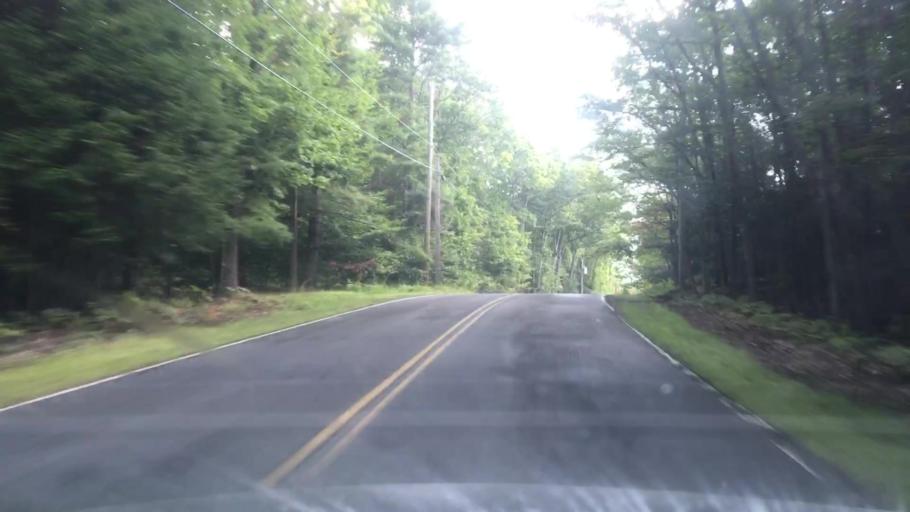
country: US
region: Maine
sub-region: Kennebec County
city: Gardiner
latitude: 44.1655
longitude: -69.7920
